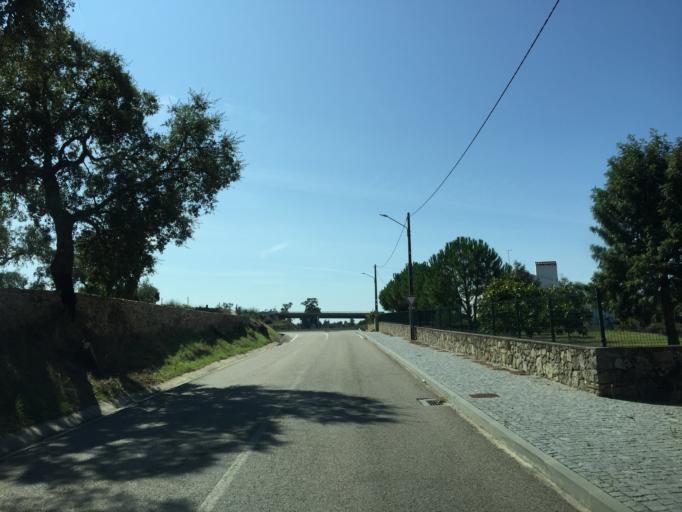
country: PT
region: Portalegre
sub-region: Portalegre
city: Alagoa
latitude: 39.4125
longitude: -7.6223
